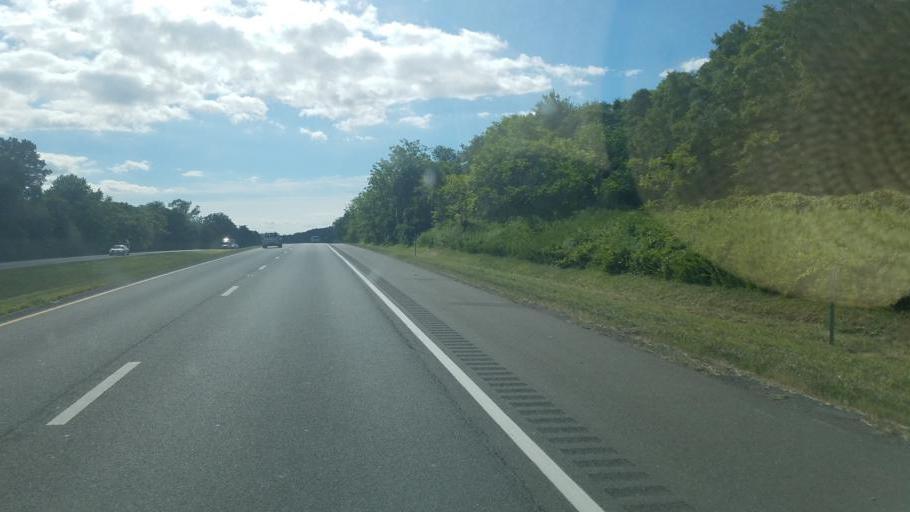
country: US
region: Virginia
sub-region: Fauquier County
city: Marshall
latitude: 38.9064
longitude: -77.9533
